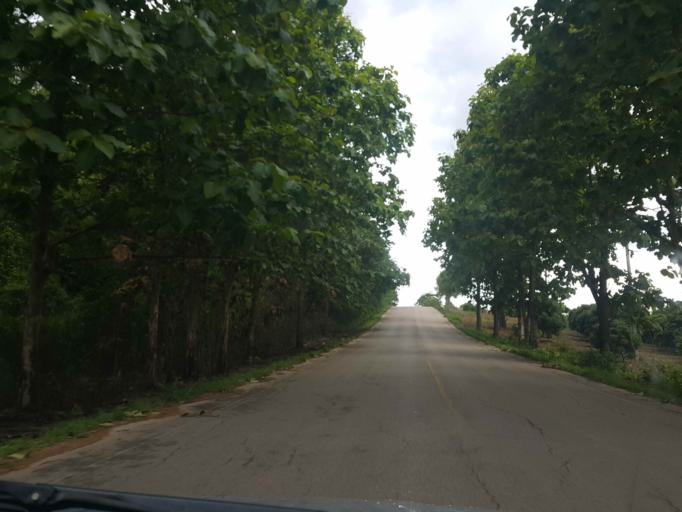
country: TH
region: Phayao
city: Dok Kham Tai
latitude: 18.9792
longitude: 100.0701
